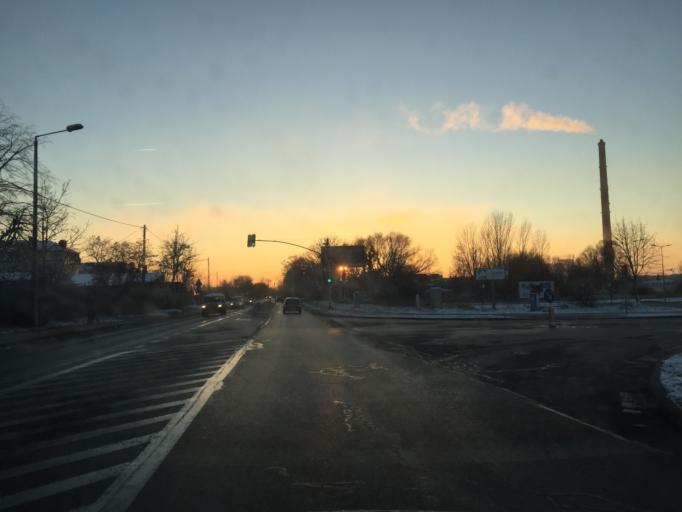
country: PL
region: Kujawsko-Pomorskie
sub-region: Powiat torunski
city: Lubicz Dolny
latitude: 53.0511
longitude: 18.7071
